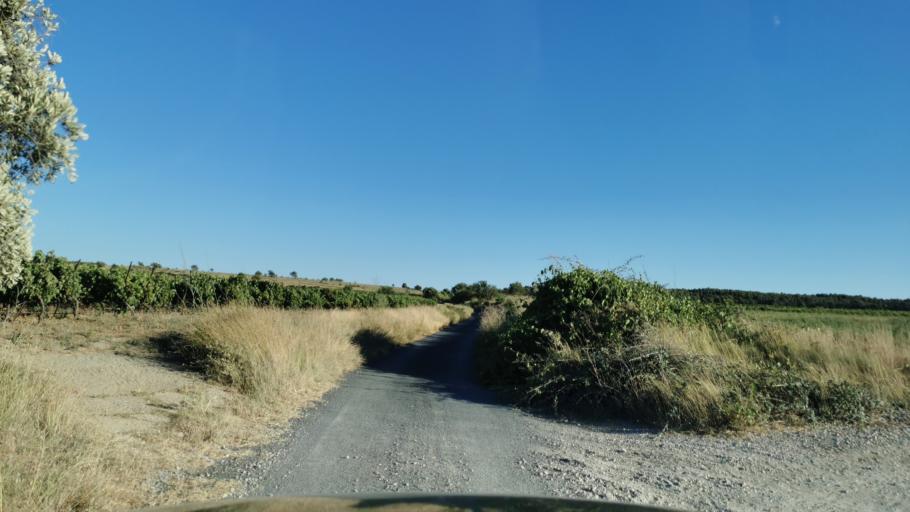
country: FR
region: Languedoc-Roussillon
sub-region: Departement de l'Aude
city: Ouveillan
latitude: 43.2779
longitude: 2.9764
